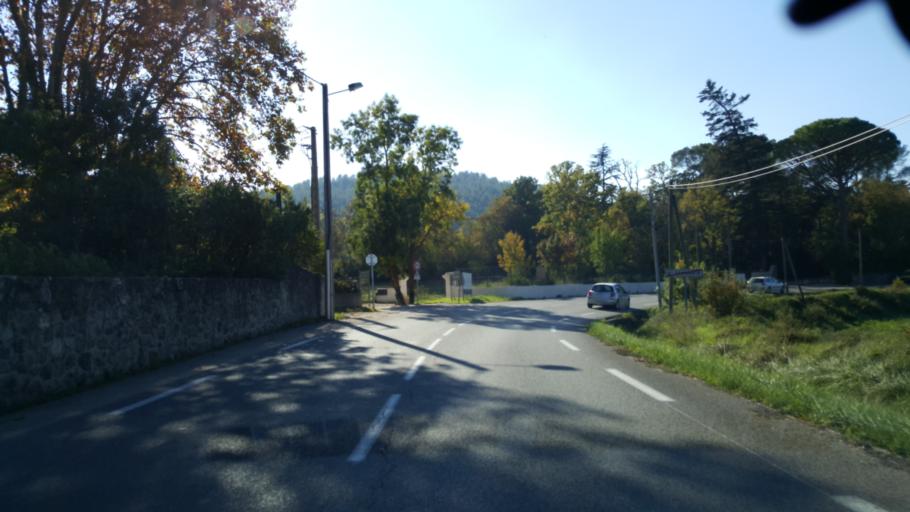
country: FR
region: Provence-Alpes-Cote d'Azur
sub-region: Departement du Var
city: Saint-Zacharie
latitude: 43.3790
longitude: 5.6980
